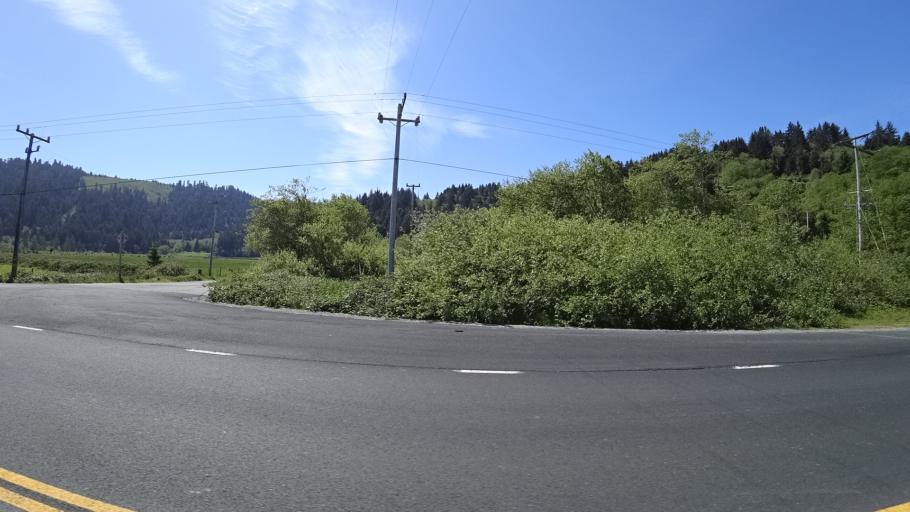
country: US
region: California
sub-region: Humboldt County
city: Westhaven-Moonstone
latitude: 41.2848
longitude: -124.0760
